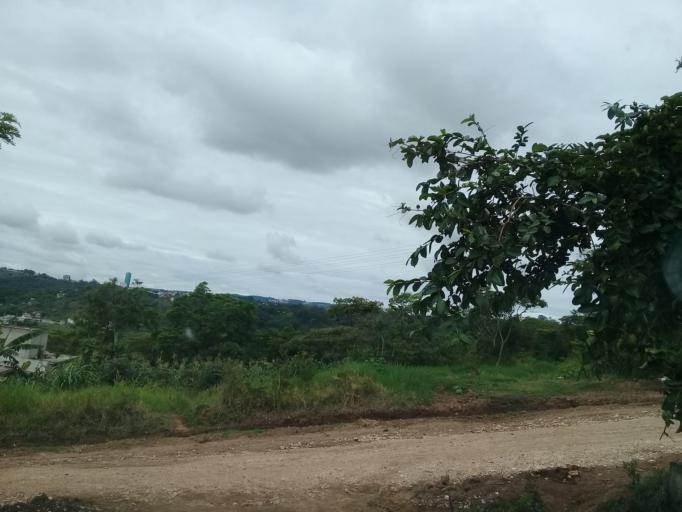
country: MX
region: Veracruz
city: El Castillo
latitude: 19.5539
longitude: -96.8799
